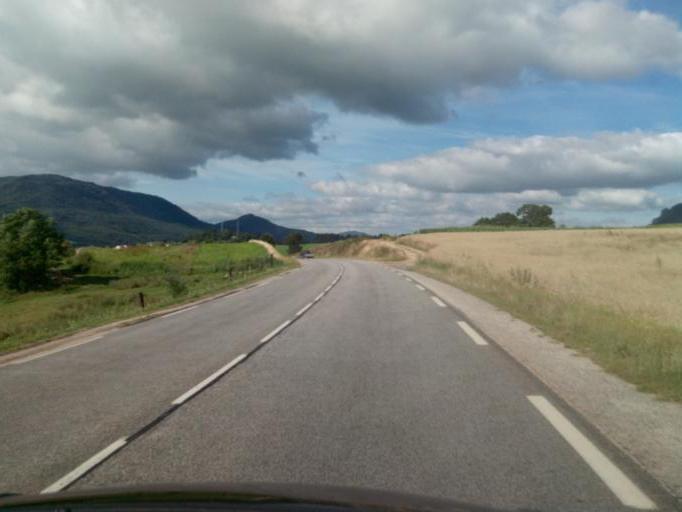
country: FR
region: Auvergne
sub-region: Departement de la Haute-Loire
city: Retournac
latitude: 45.2244
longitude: 4.0287
